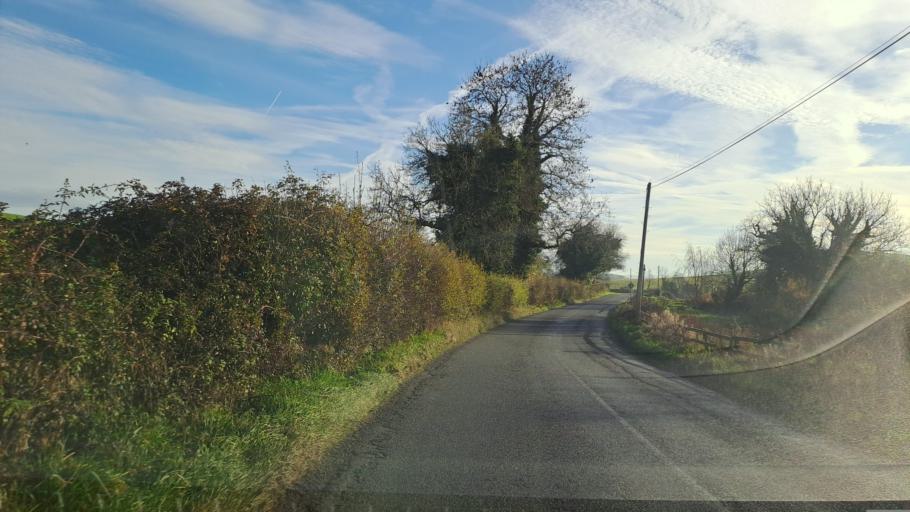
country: IE
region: Ulster
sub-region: County Monaghan
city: Carrickmacross
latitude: 53.8609
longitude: -6.6777
